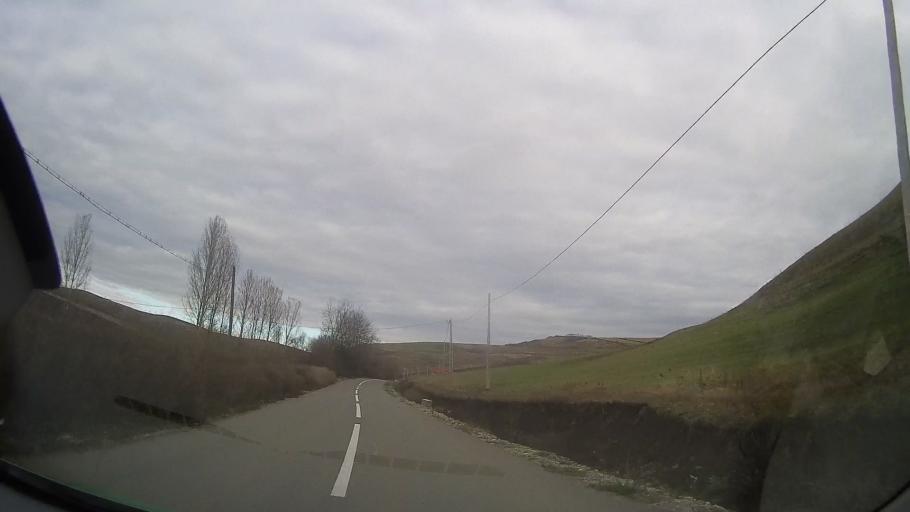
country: RO
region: Bistrita-Nasaud
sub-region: Comuna Silvasu de Campie
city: Silvasu de Campie
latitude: 46.8118
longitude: 24.2956
